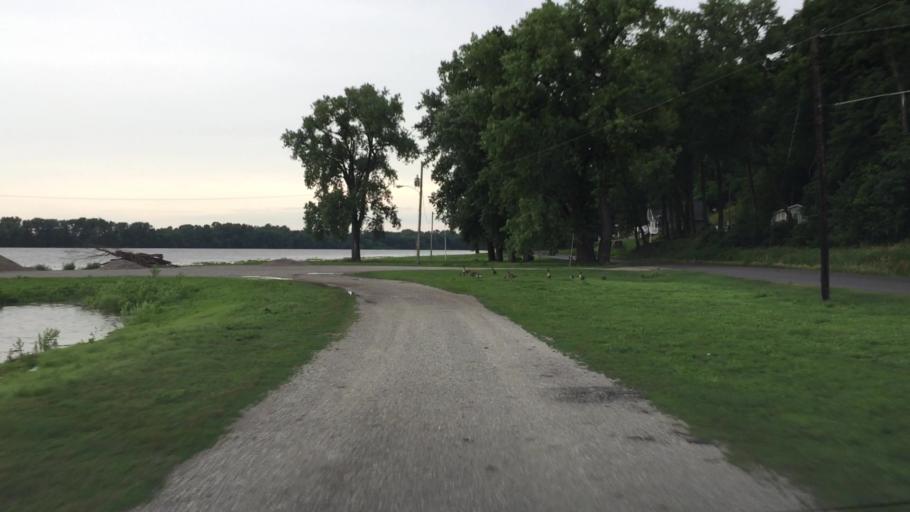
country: US
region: Illinois
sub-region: Hancock County
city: Warsaw
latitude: 40.3541
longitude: -91.4457
